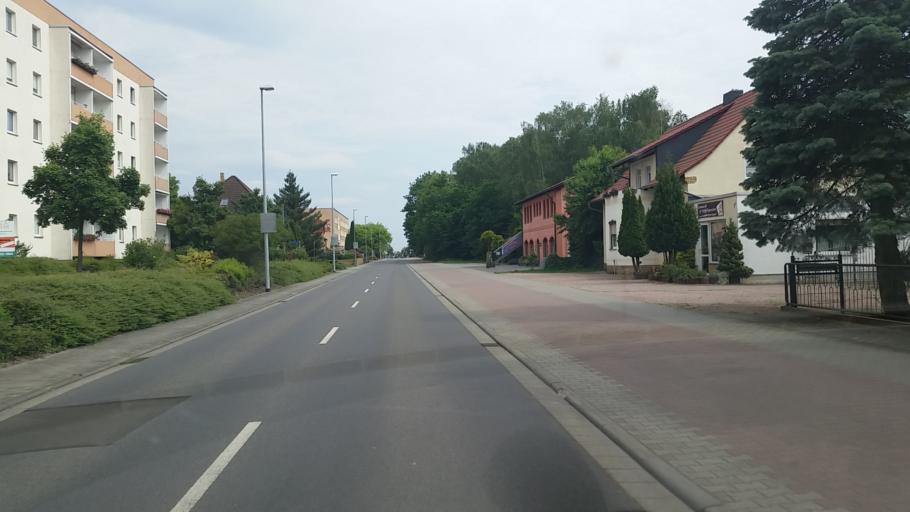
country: DE
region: Brandenburg
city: Schwarzheide
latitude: 51.4837
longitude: 13.8402
